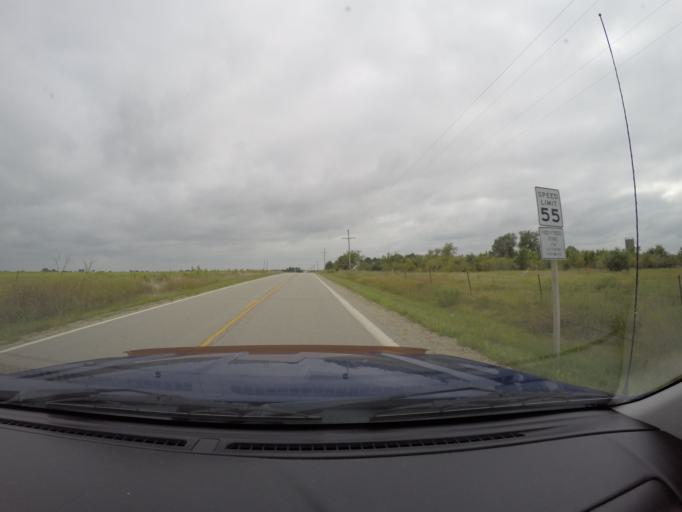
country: US
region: Kansas
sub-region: Morris County
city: Council Grove
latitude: 38.8376
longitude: -96.5941
